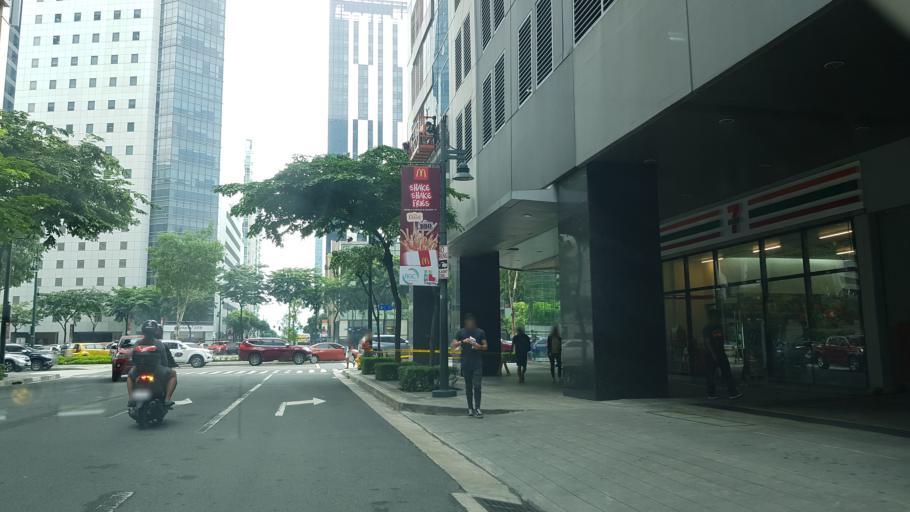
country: PH
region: Metro Manila
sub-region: Makati City
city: Makati City
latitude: 14.5537
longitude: 121.0470
